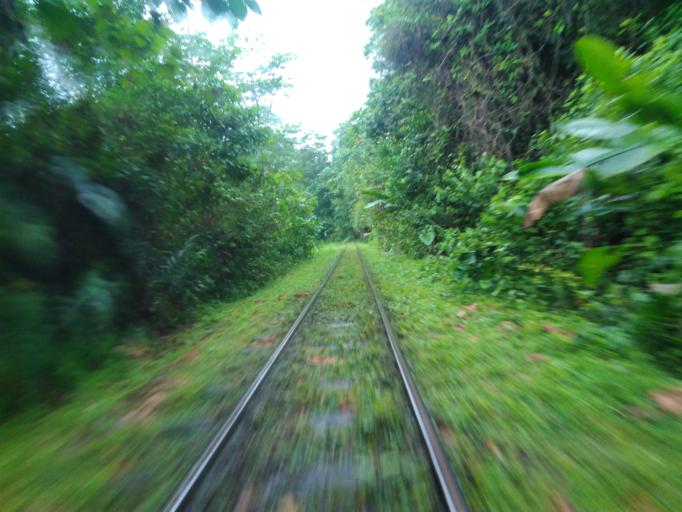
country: CO
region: Valle del Cauca
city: Buenaventura
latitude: 3.8439
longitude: -76.8804
